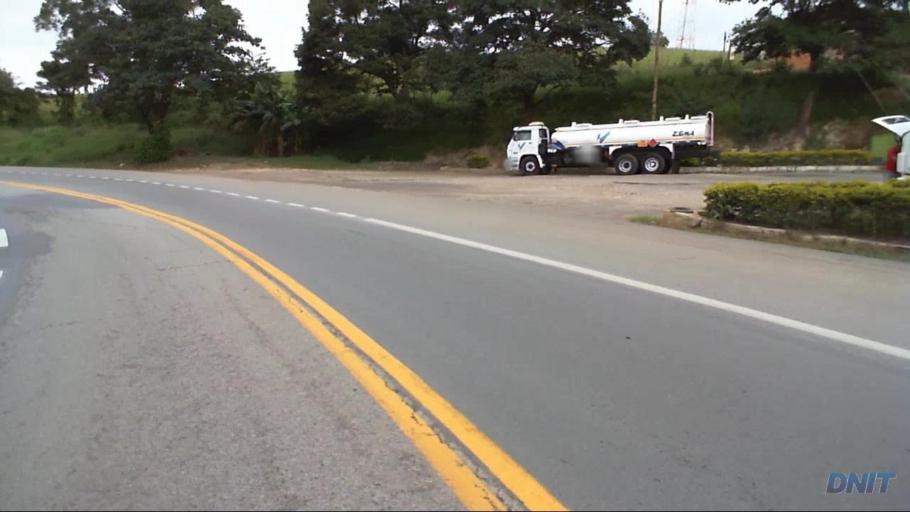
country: BR
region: Minas Gerais
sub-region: Caete
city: Caete
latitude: -19.7528
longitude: -43.5391
